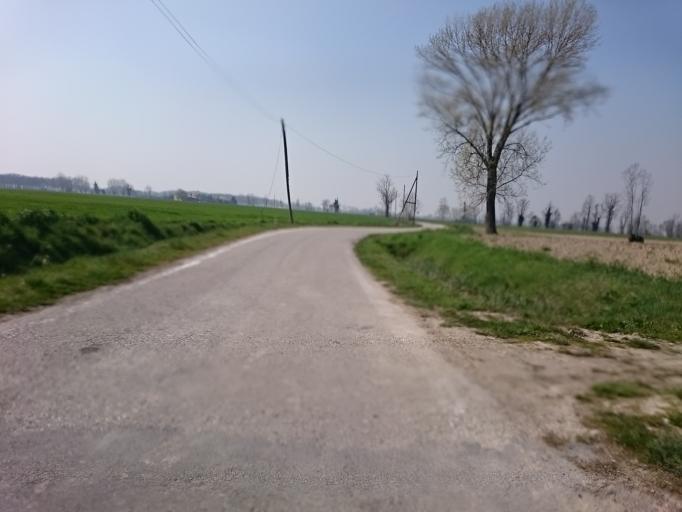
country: IT
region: Veneto
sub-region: Provincia di Padova
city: Sant'Elena
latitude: 45.1904
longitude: 11.6994
